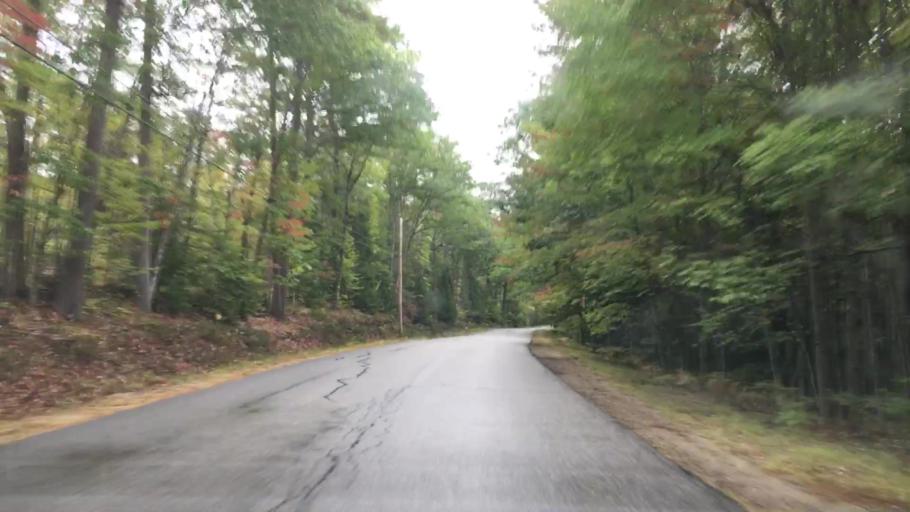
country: US
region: Maine
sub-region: Cumberland County
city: Harrison
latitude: 44.0504
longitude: -70.6172
